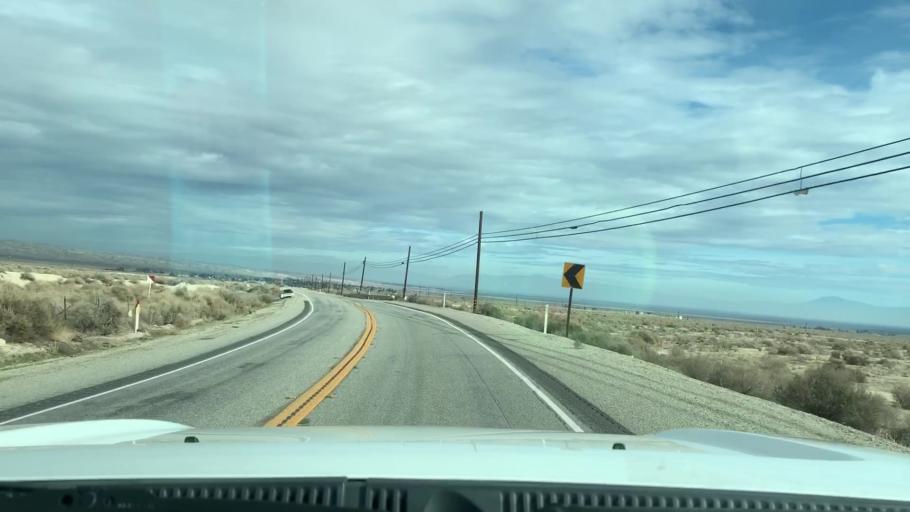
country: US
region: California
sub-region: Kern County
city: Ford City
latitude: 35.1884
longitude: -119.4369
